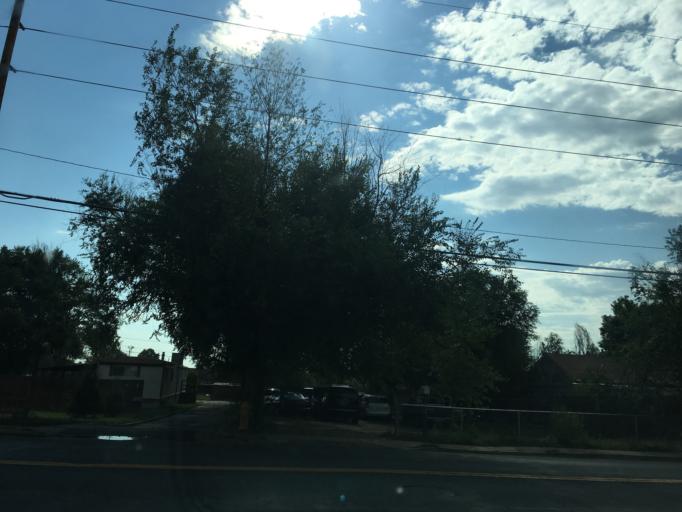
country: US
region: Colorado
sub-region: Arapahoe County
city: Sheridan
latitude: 39.6978
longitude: -105.0299
